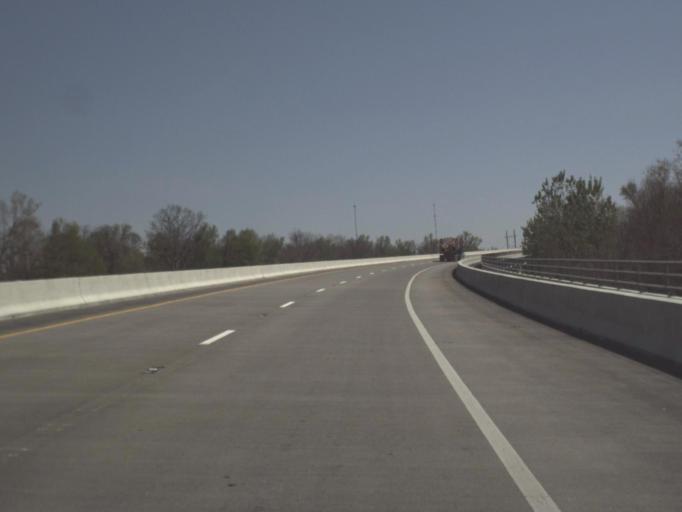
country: US
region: Florida
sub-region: Liberty County
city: Bristol
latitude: 30.4413
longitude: -85.0045
